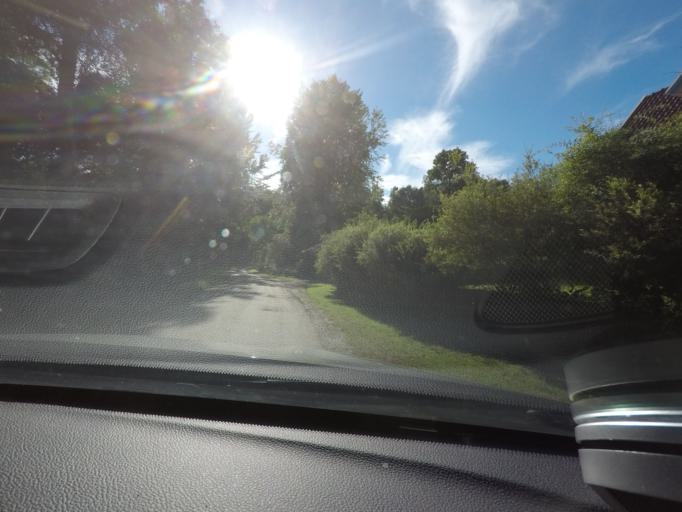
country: SE
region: Skane
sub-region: Hassleholms Kommun
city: Hassleholm
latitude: 56.1173
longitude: 13.8169
